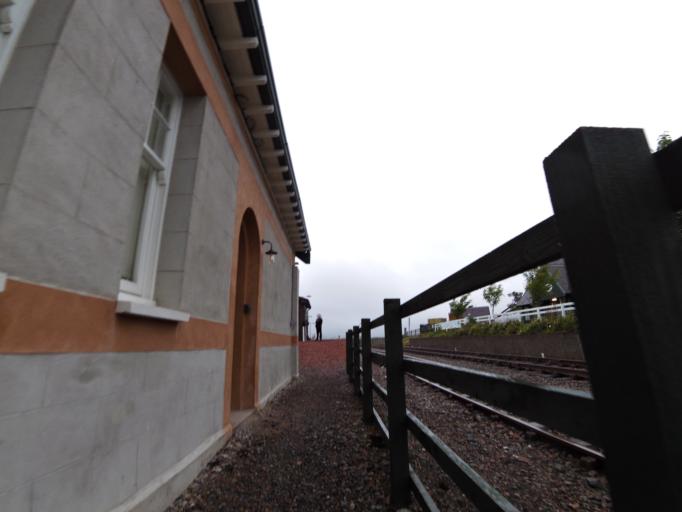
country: GB
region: Scotland
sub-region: Highland
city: Spean Bridge
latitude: 56.7601
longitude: -4.6904
